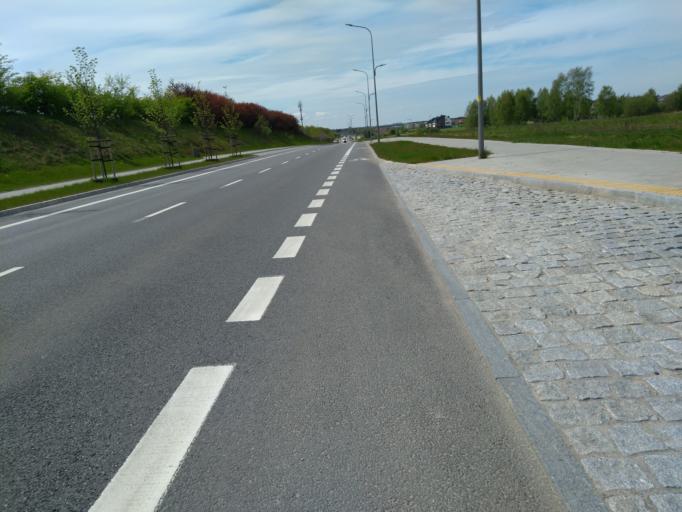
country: PL
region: Pomeranian Voivodeship
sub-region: Gdynia
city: Wielki Kack
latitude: 54.4163
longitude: 18.4777
